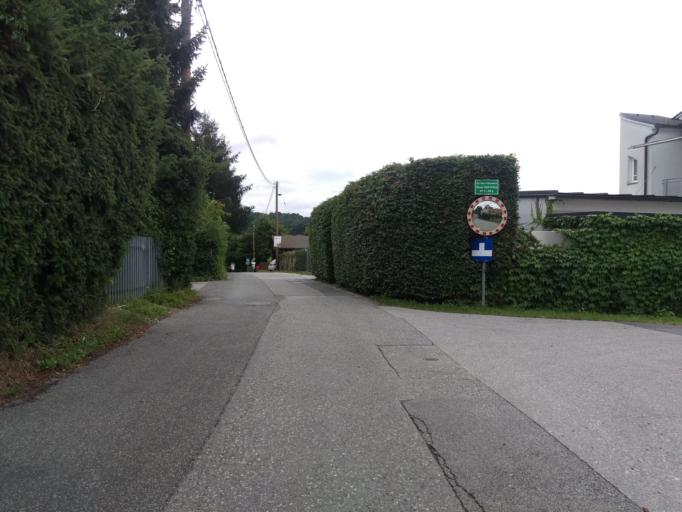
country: AT
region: Styria
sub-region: Politischer Bezirk Graz-Umgebung
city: Hart bei Graz
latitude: 47.0650
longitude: 15.4919
